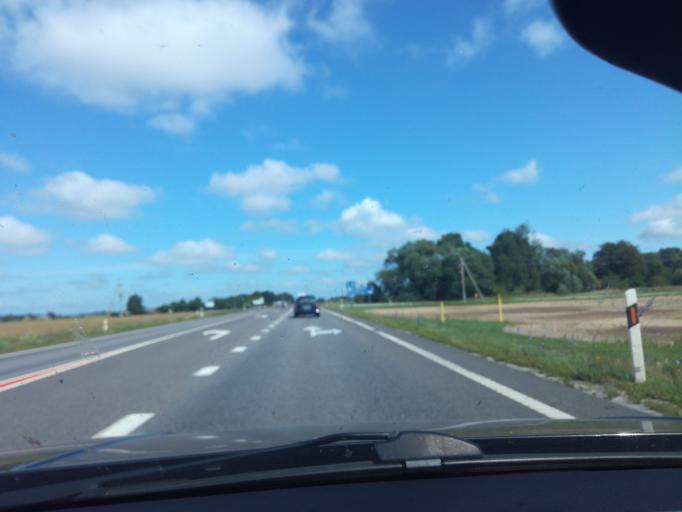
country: LT
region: Panevezys
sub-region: Panevezys City
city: Panevezys
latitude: 55.8549
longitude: 24.3501
